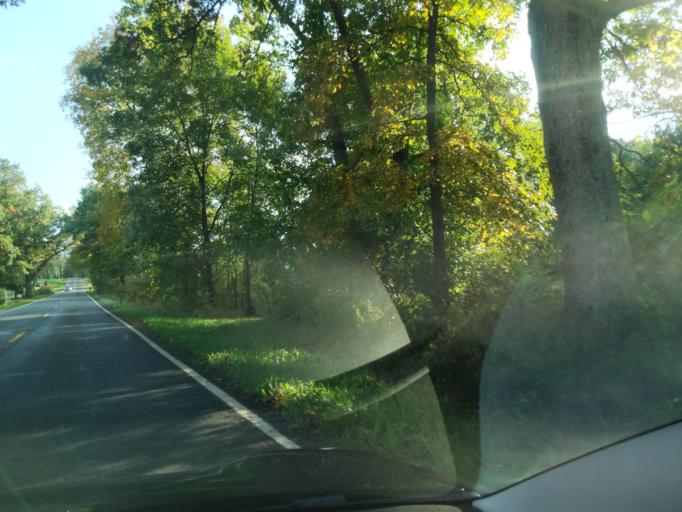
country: US
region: Michigan
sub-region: Ingham County
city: Leslie
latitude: 42.3642
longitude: -84.4629
